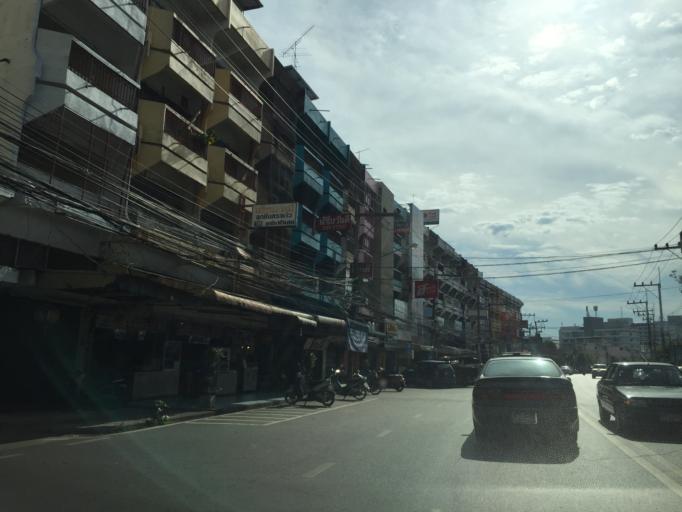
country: TH
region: Phitsanulok
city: Phitsanulok
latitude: 16.8202
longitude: 100.2699
